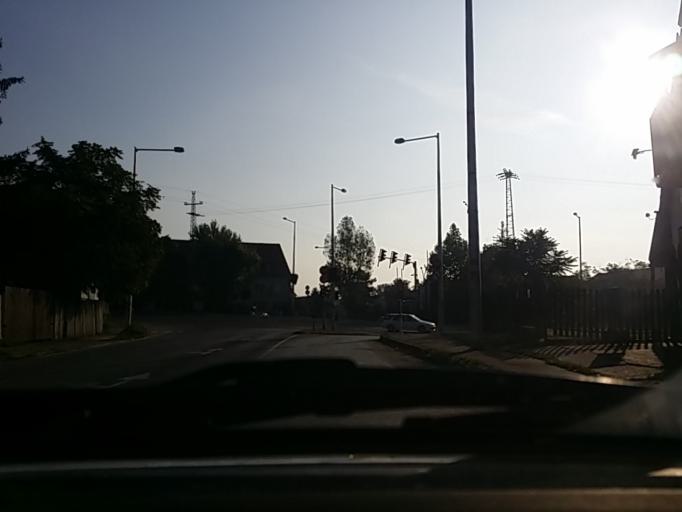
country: HU
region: Pest
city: Szentendre
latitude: 47.6711
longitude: 19.0721
